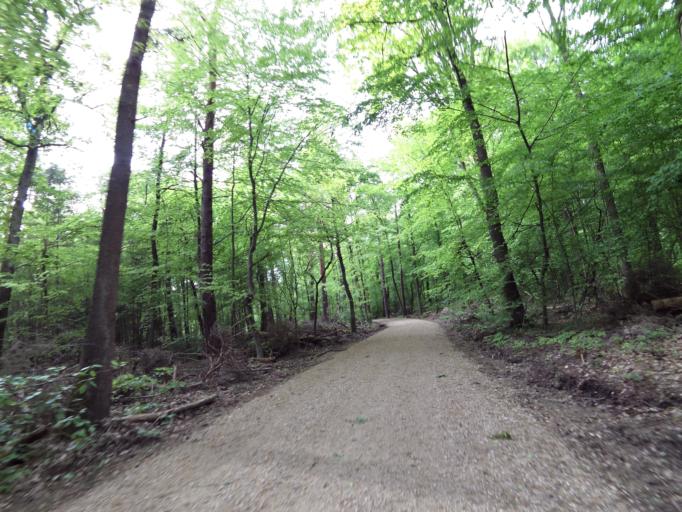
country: DE
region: North Rhine-Westphalia
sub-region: Regierungsbezirk Koln
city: Bonn
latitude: 50.6904
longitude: 7.0979
